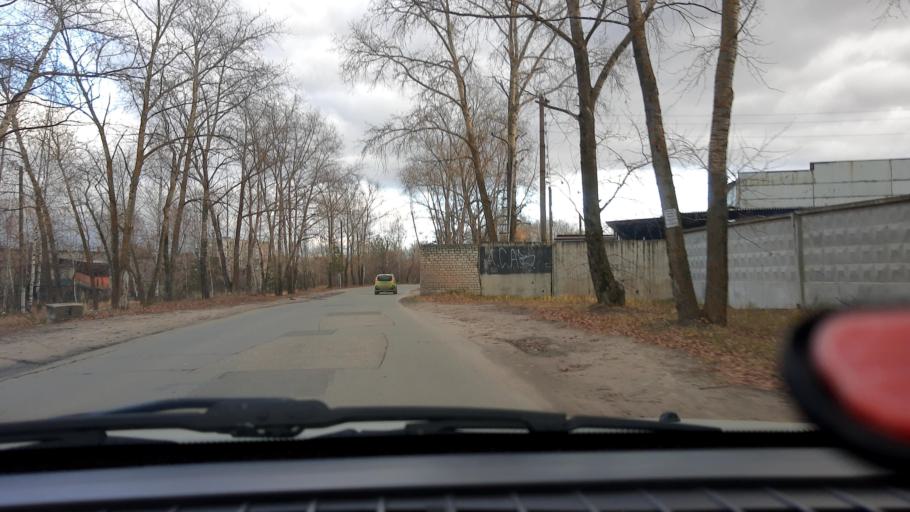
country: RU
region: Nizjnij Novgorod
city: Gorbatovka
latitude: 56.3575
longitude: 43.7996
